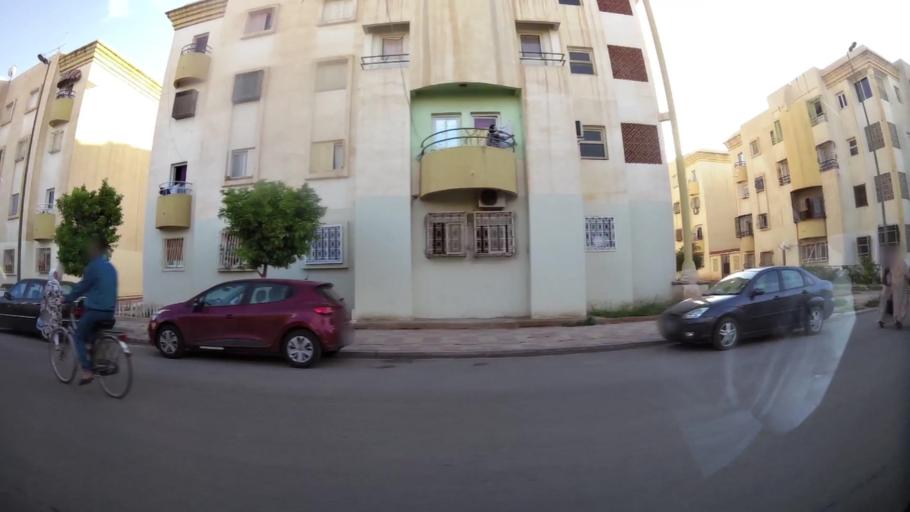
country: MA
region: Oriental
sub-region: Oujda-Angad
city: Oujda
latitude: 34.6996
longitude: -1.9144
